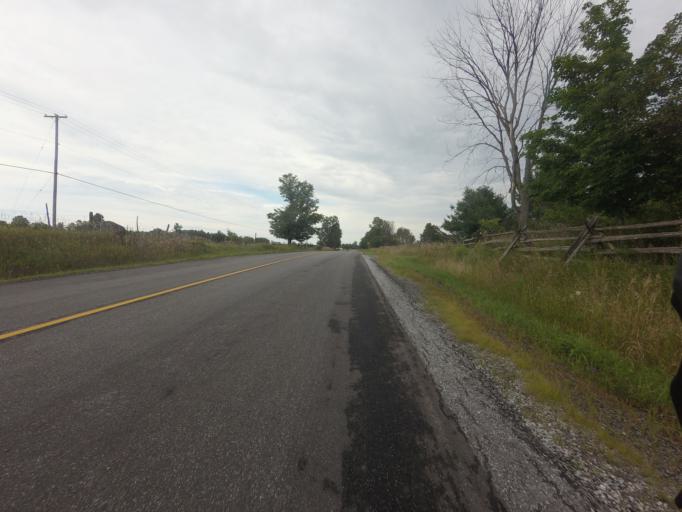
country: CA
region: Ontario
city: Perth
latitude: 45.0647
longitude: -76.3891
